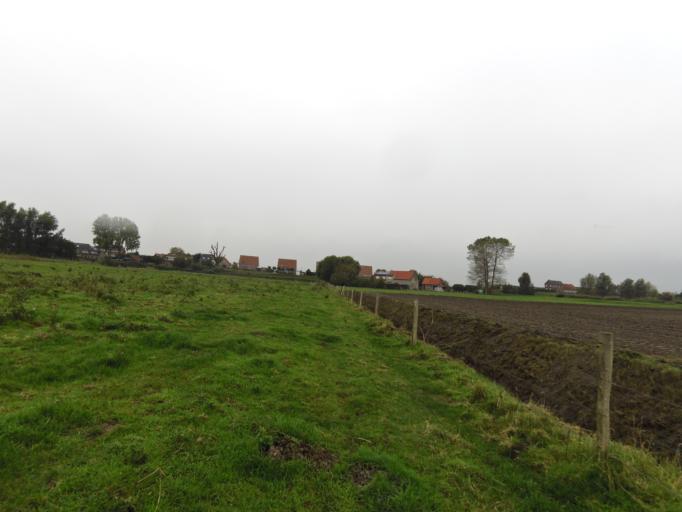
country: NL
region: North Brabant
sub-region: Gemeente Steenbergen
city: Dinteloord
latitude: 51.6783
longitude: 4.2830
